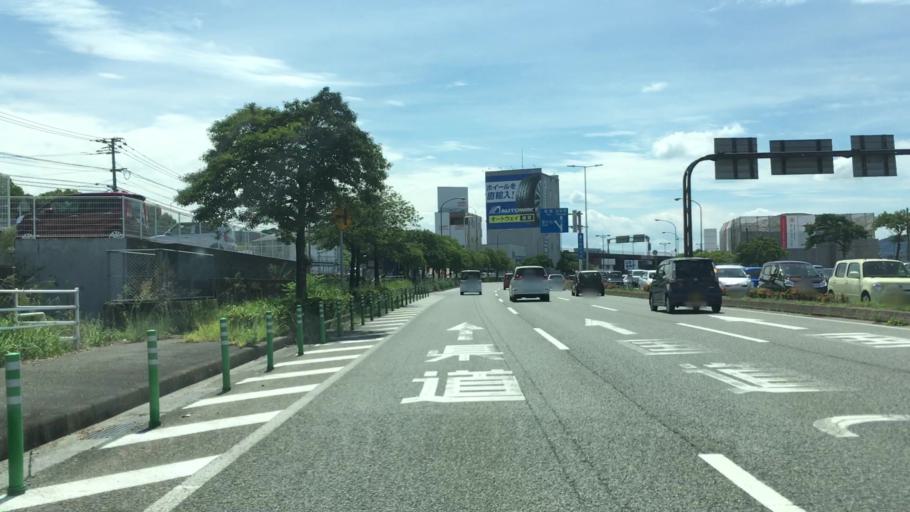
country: JP
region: Fukuoka
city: Onojo
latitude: 33.5285
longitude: 130.4942
